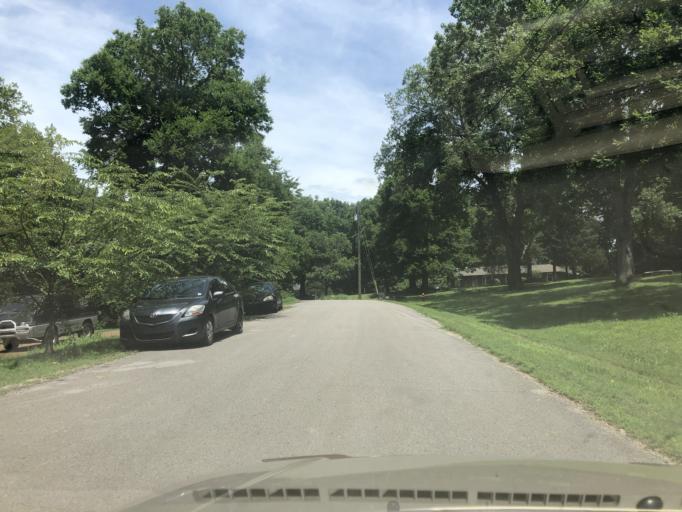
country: US
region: Tennessee
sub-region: Davidson County
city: Lakewood
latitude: 36.2446
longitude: -86.6827
